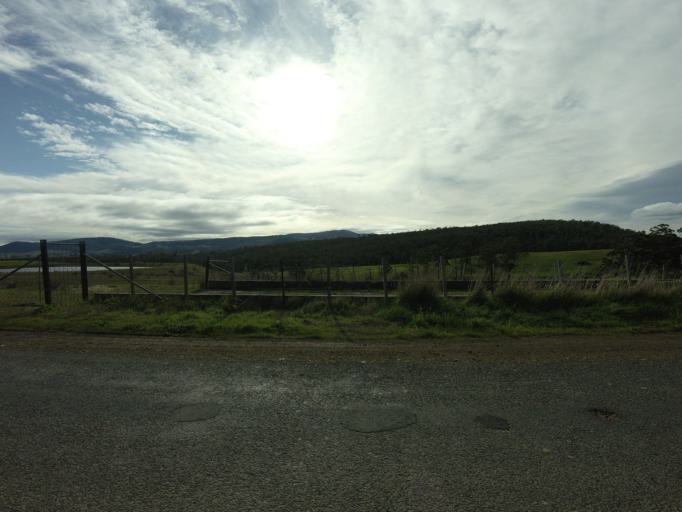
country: AU
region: Tasmania
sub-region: Derwent Valley
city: New Norfolk
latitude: -42.7814
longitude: 146.9916
